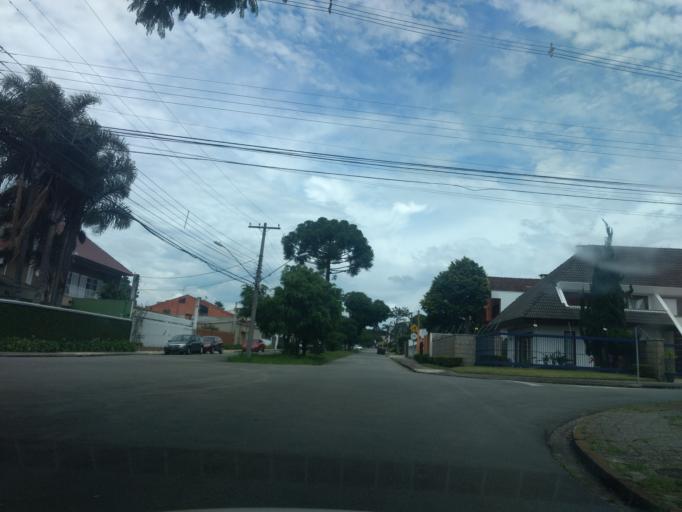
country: BR
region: Parana
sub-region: Pinhais
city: Pinhais
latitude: -25.4184
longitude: -49.2281
